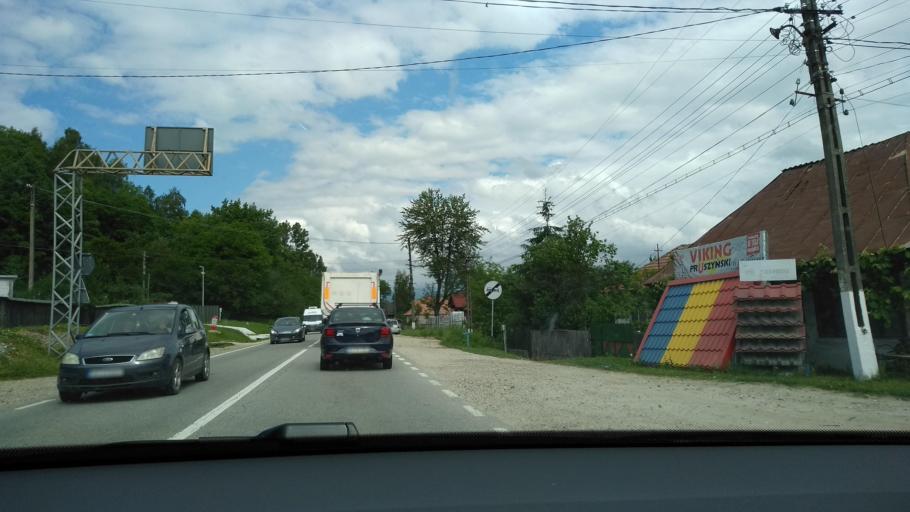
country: RO
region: Valcea
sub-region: Comuna Tomsani
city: Tomsani
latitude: 45.1305
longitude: 24.0358
